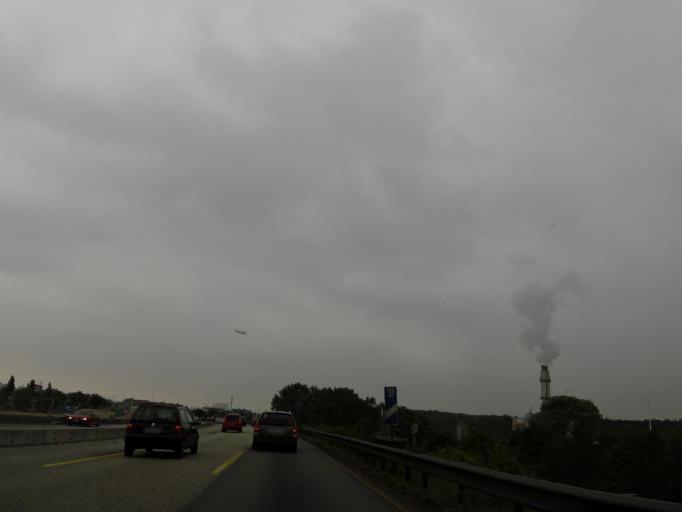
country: DE
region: Hamburg
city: Stellingen
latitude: 53.5886
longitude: 9.9153
